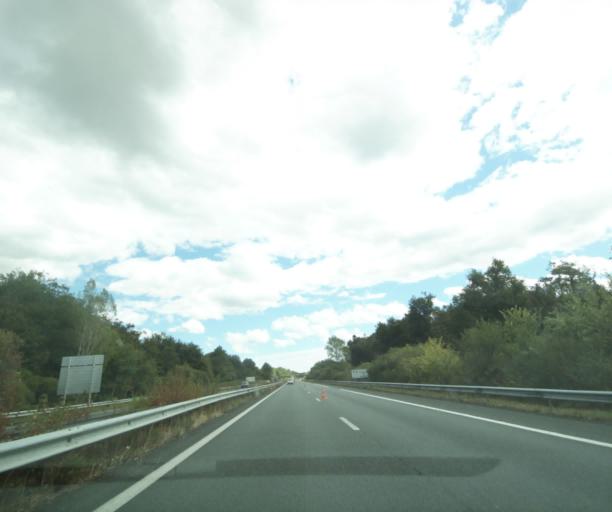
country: FR
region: Aquitaine
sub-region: Departement de la Gironde
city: La Reole
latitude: 44.5108
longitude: -0.0599
